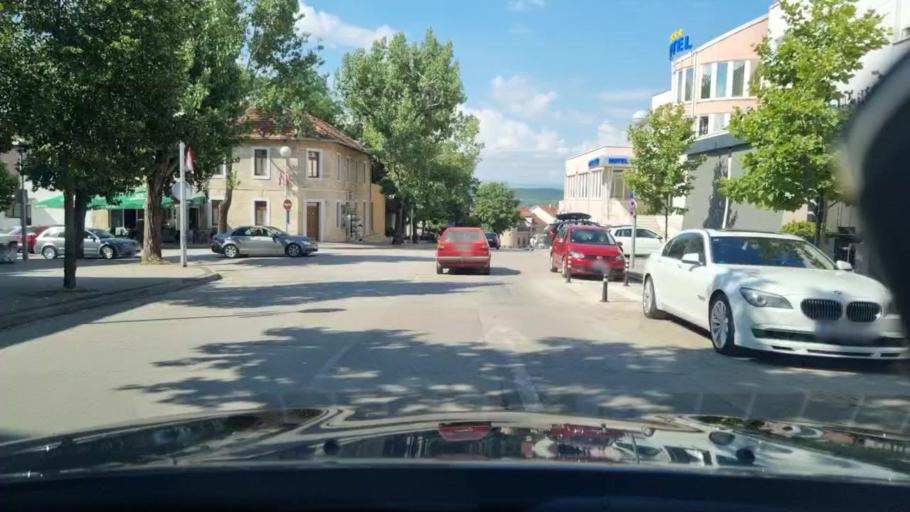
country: BA
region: Federation of Bosnia and Herzegovina
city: Dreznica
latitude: 43.4734
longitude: 17.3263
